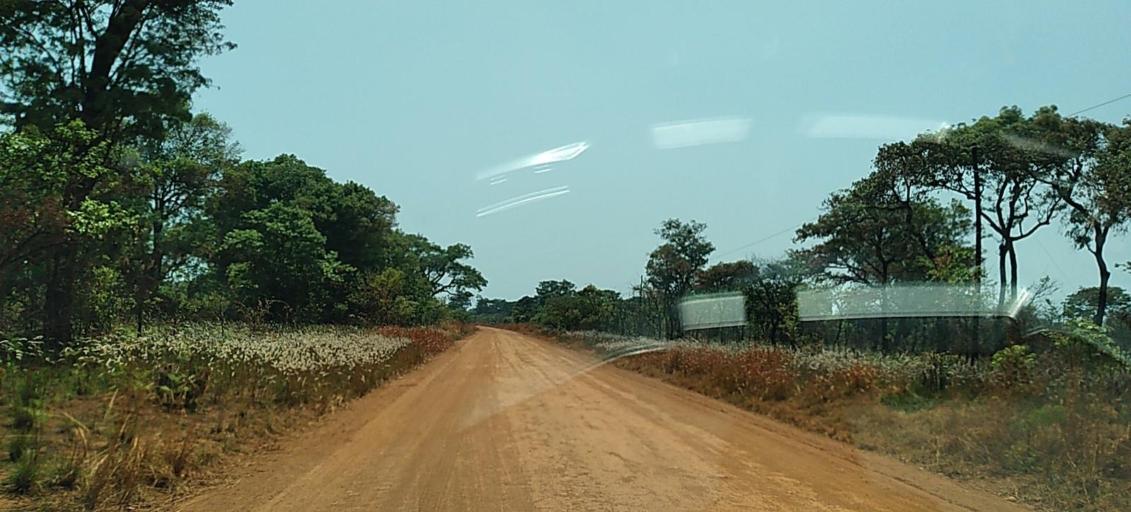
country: CD
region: Katanga
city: Kipushi
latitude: -11.9837
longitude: 26.8831
